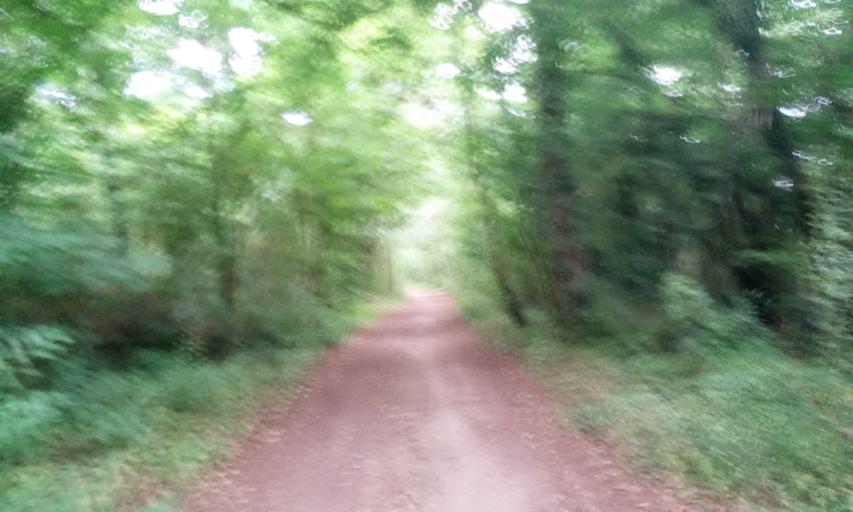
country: FR
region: Lower Normandy
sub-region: Departement du Calvados
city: Bellengreville
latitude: 49.1169
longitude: -0.2036
